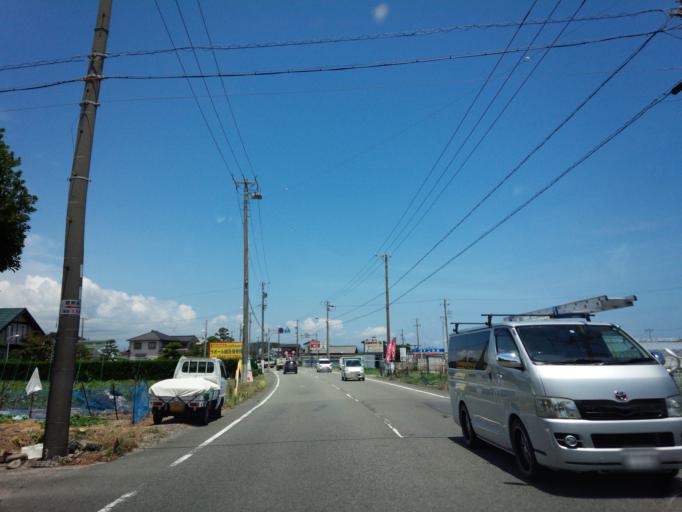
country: JP
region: Shizuoka
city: Sagara
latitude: 34.7216
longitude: 138.2191
